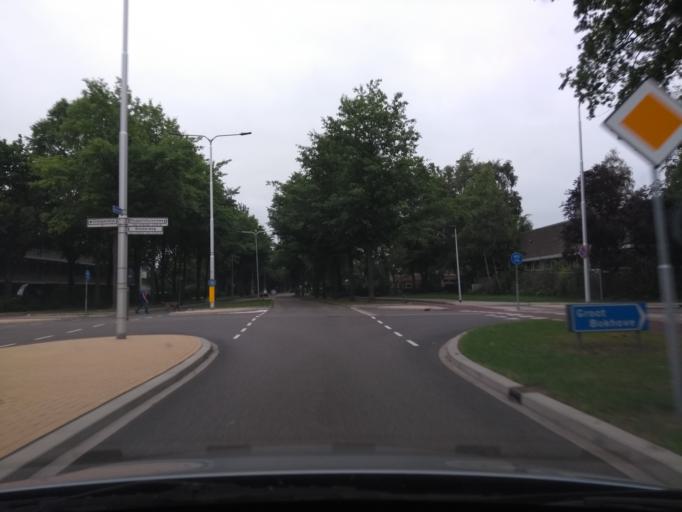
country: NL
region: Overijssel
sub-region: Gemeente Almelo
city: Almelo
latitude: 52.3725
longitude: 6.6784
